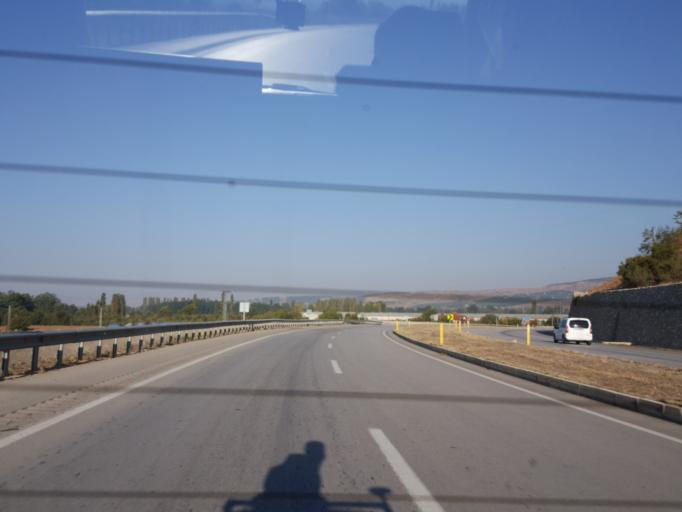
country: TR
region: Amasya
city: Amasya
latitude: 40.5583
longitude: 35.7944
